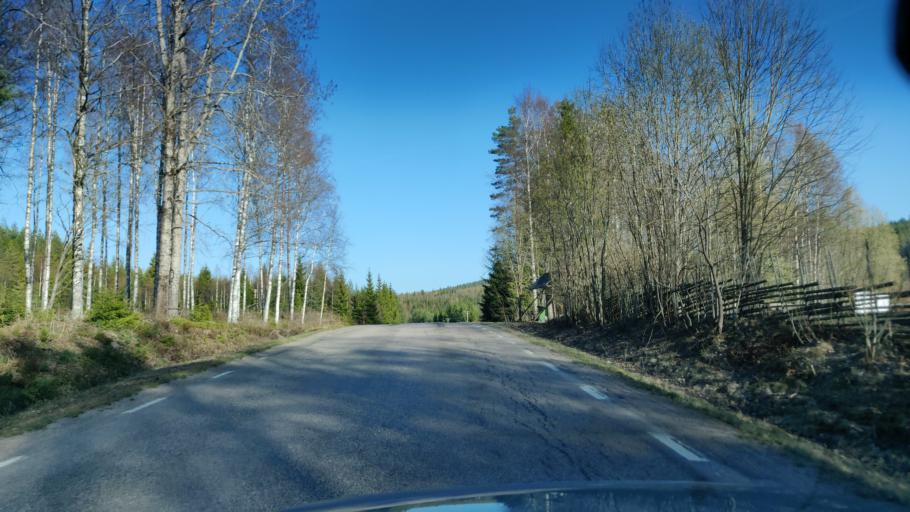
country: SE
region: Vaermland
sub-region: Munkfors Kommun
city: Munkfors
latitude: 59.9823
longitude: 13.3589
